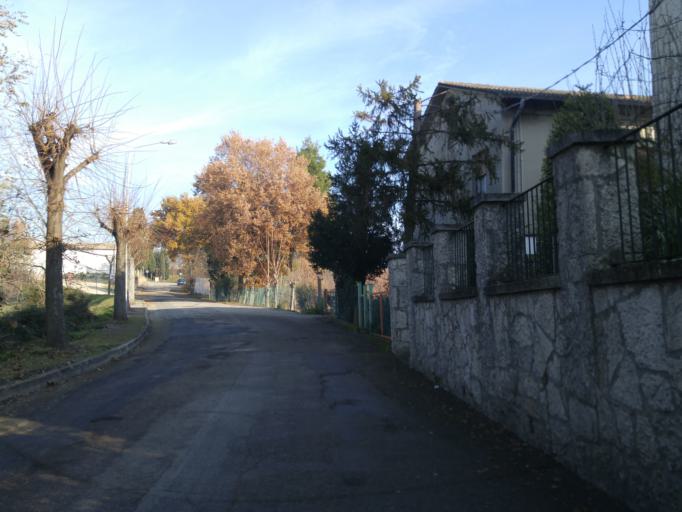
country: IT
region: The Marches
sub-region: Provincia di Pesaro e Urbino
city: Villanova
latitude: 43.7099
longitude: 12.9148
